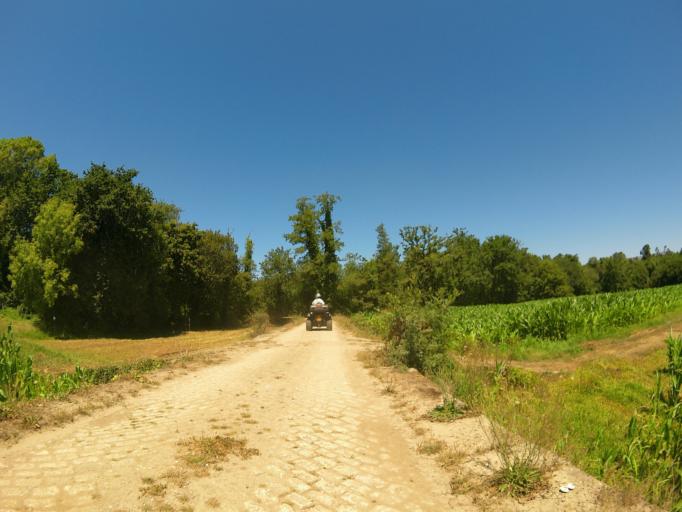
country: PT
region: Viana do Castelo
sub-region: Viana do Castelo
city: Darque
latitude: 41.7145
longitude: -8.7122
